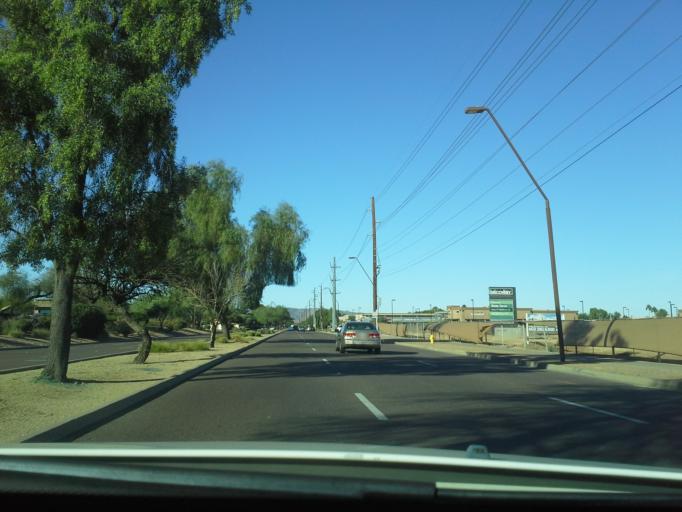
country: US
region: Arizona
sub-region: Maricopa County
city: San Carlos
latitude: 33.3493
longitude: -111.8992
